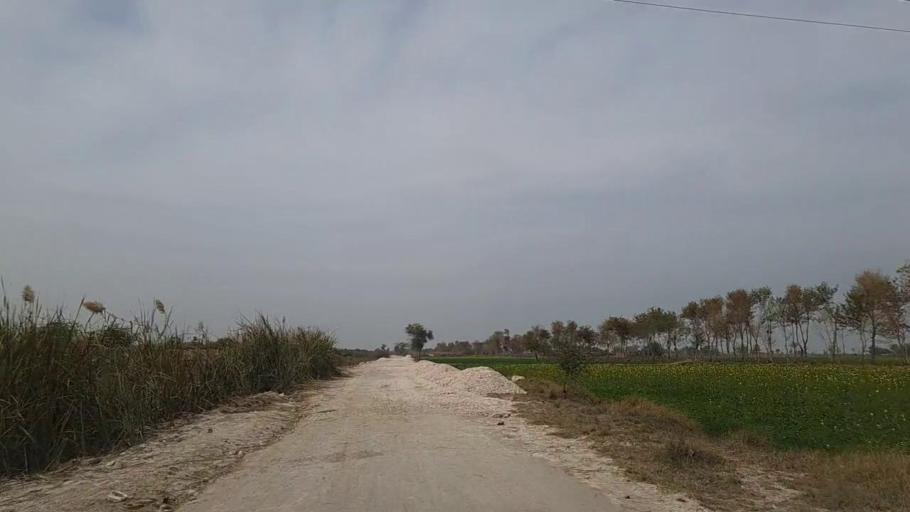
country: PK
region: Sindh
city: Daur
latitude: 26.4163
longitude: 68.4252
